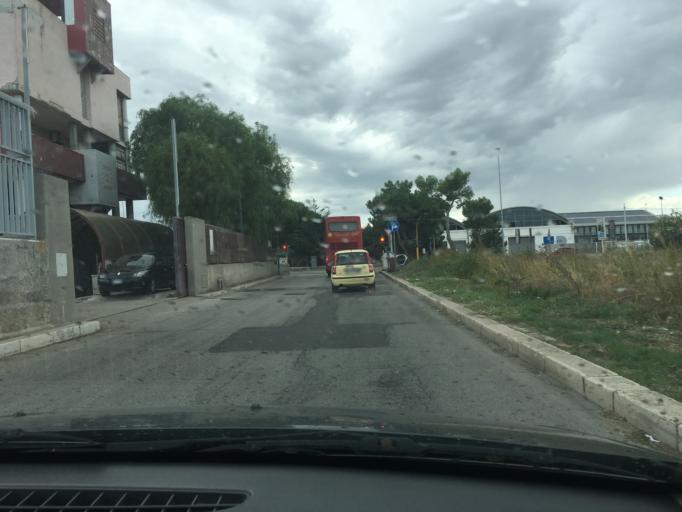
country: IT
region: Apulia
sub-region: Provincia di Bari
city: San Paolo
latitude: 41.1336
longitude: 16.8229
